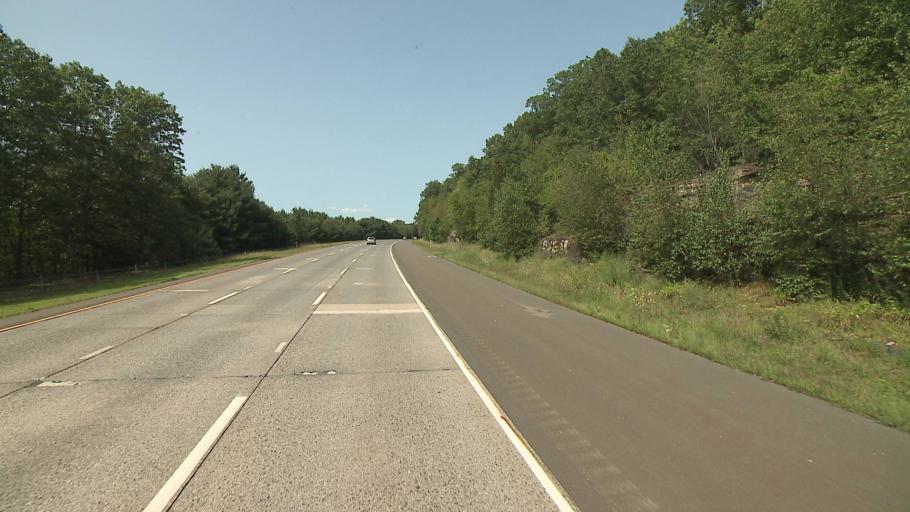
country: US
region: Connecticut
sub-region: Fairfield County
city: Trumbull
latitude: 41.2616
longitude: -73.2086
